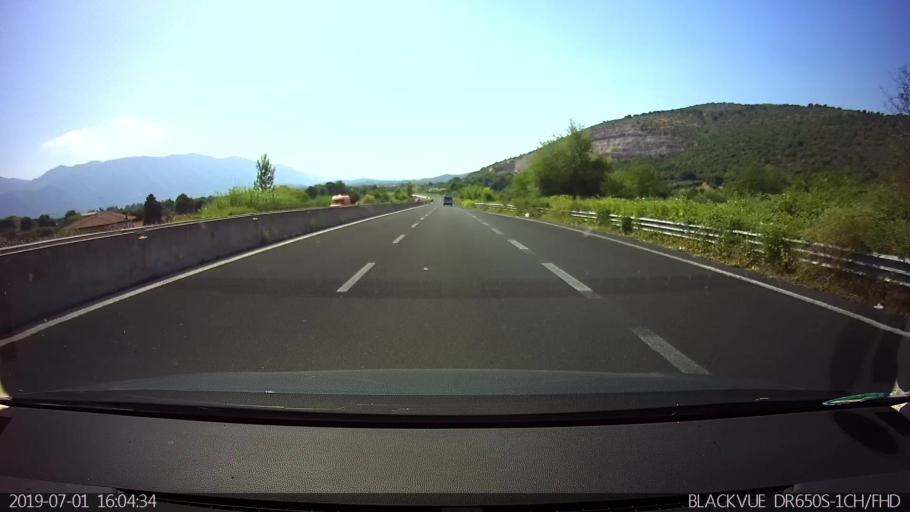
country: IT
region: Latium
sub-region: Provincia di Frosinone
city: Tecchiena
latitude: 41.6710
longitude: 13.3099
